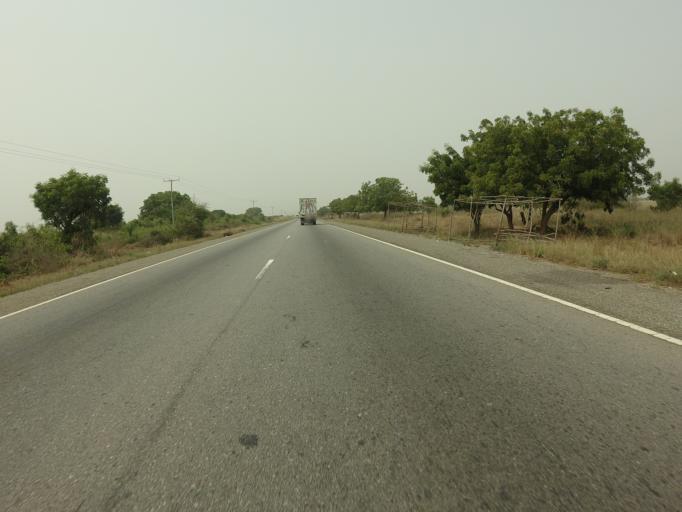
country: GH
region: Volta
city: Anloga
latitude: 5.8872
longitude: 0.4525
